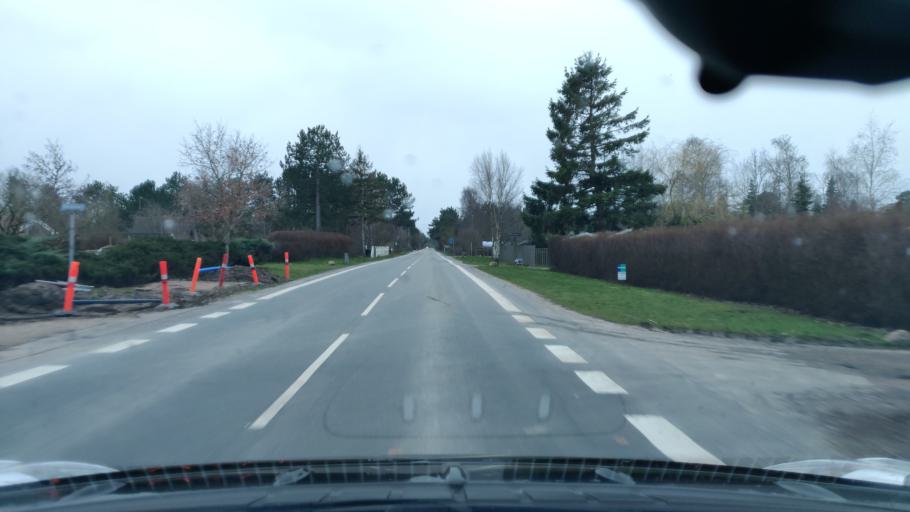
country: DK
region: Zealand
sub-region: Odsherred Kommune
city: Hojby
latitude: 55.8765
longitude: 11.5438
